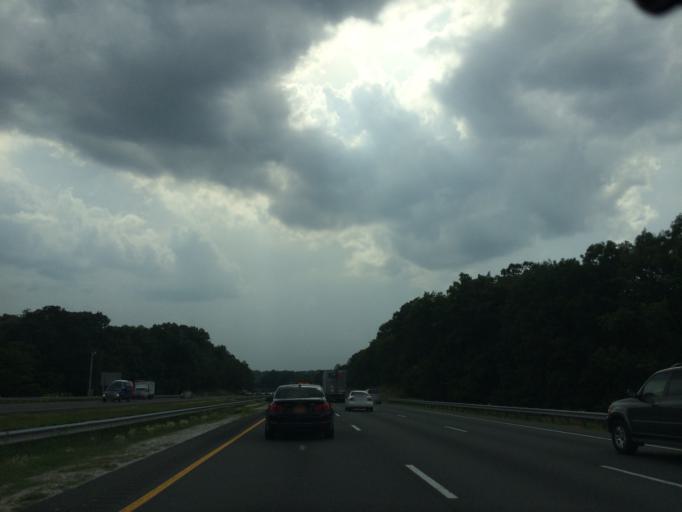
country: US
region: Maryland
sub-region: Baltimore County
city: Milford Mill
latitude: 39.3070
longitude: -76.7789
